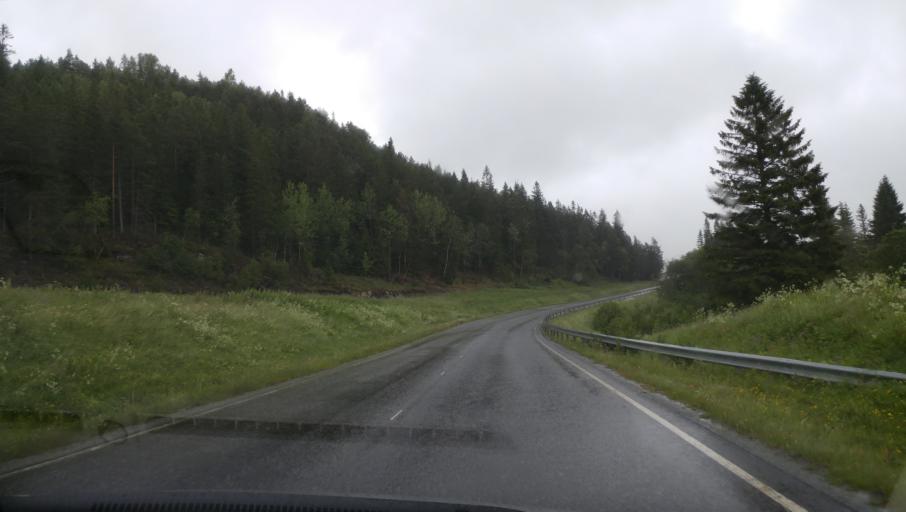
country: NO
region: Nord-Trondelag
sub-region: Stjordal
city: Stjordalshalsen
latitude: 63.3952
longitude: 11.0283
